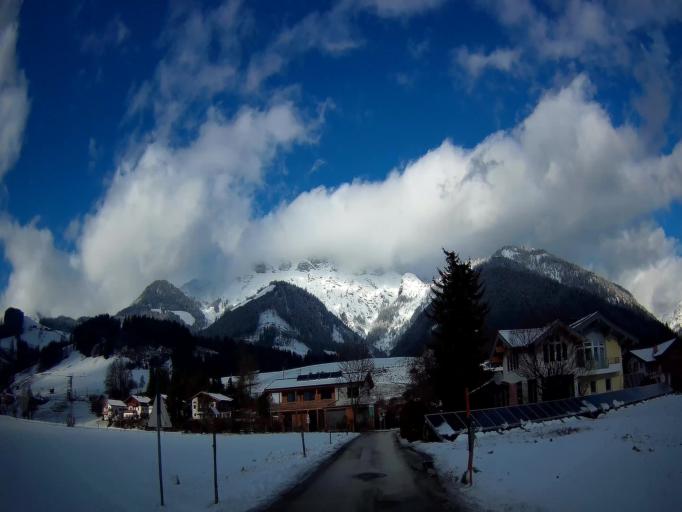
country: AT
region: Salzburg
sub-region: Politischer Bezirk Zell am See
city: Leogang
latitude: 47.4439
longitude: 12.7959
